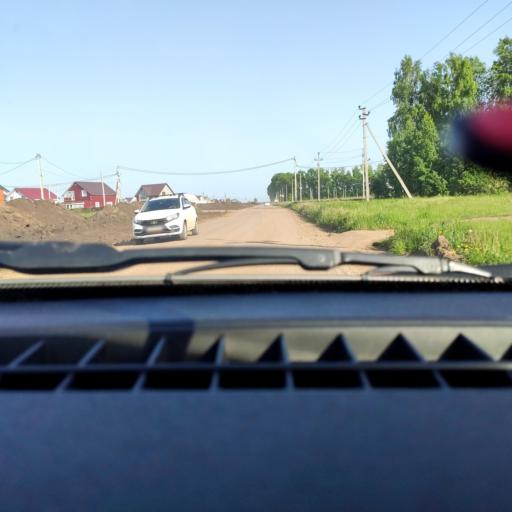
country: RU
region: Bashkortostan
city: Iglino
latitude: 54.8201
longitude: 56.4233
